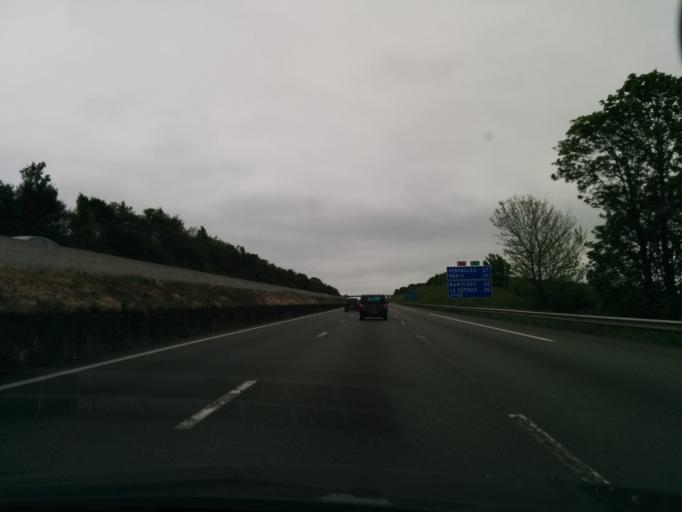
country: FR
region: Ile-de-France
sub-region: Departement des Yvelines
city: Chapet
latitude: 48.9620
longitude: 1.9287
